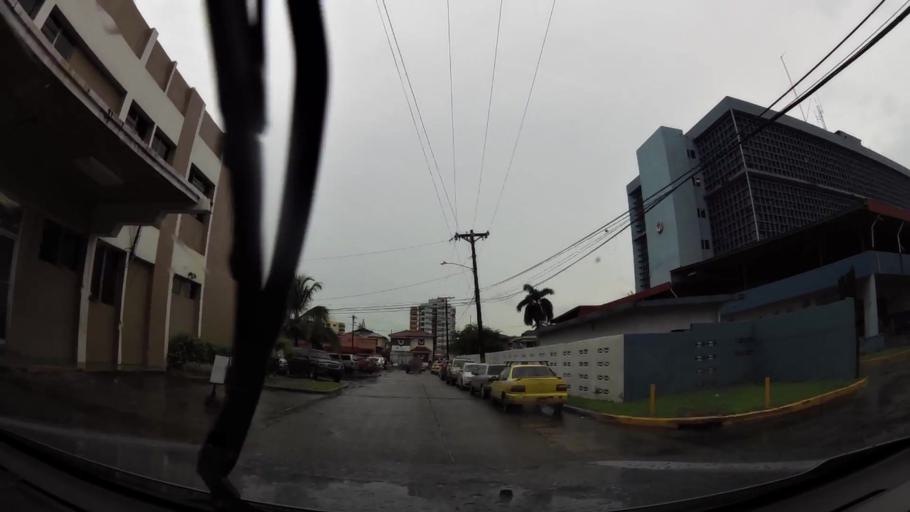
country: PA
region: Colon
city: Colon
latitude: 9.3571
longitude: -79.8940
